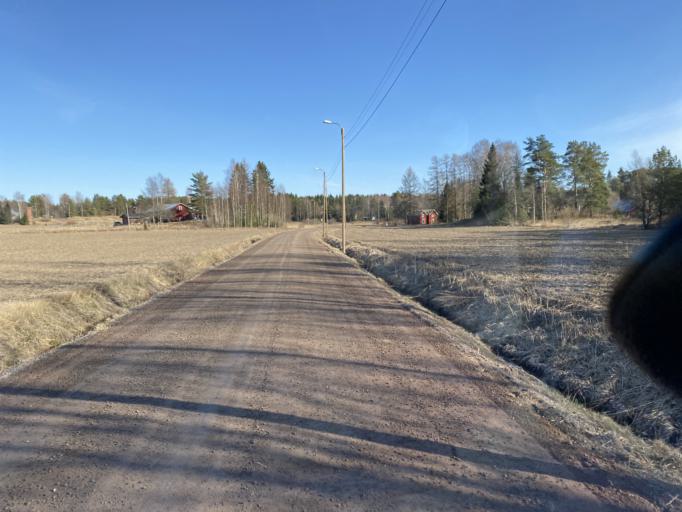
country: FI
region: Satakunta
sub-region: Rauma
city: Lappi
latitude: 61.1400
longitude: 21.9455
